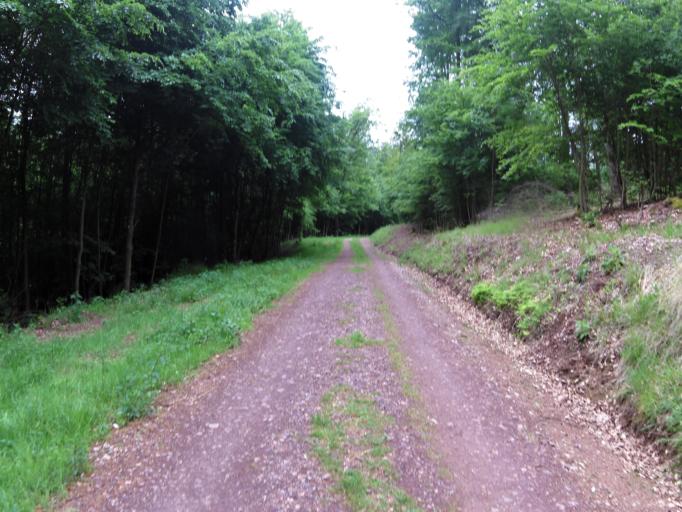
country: DE
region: Thuringia
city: Eisenach
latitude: 50.9433
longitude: 10.3196
